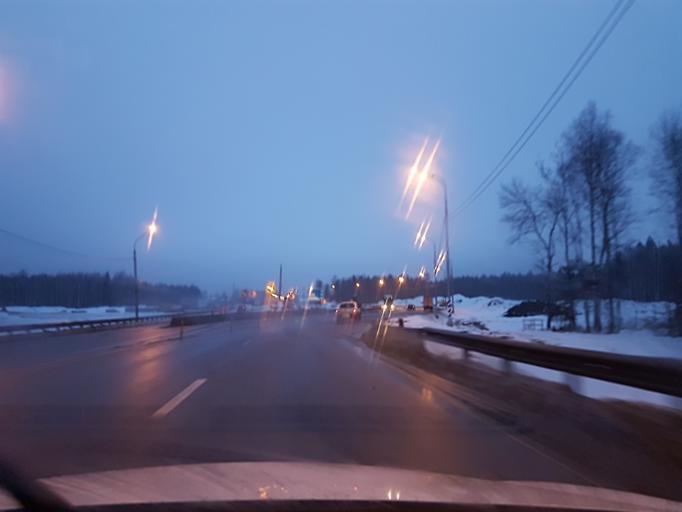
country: RU
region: Moskovskaya
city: Klin
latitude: 56.3767
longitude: 36.6775
